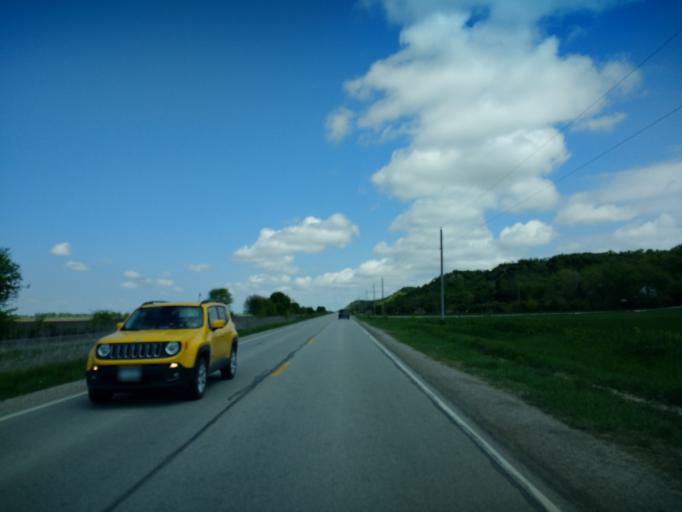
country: US
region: Iowa
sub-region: Harrison County
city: Missouri Valley
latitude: 41.4611
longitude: -95.8767
